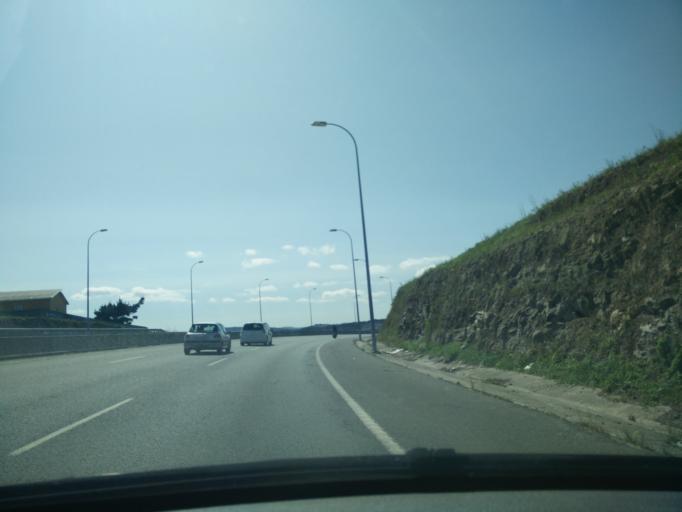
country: ES
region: Galicia
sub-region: Provincia da Coruna
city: A Coruna
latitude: 43.3605
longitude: -8.4324
